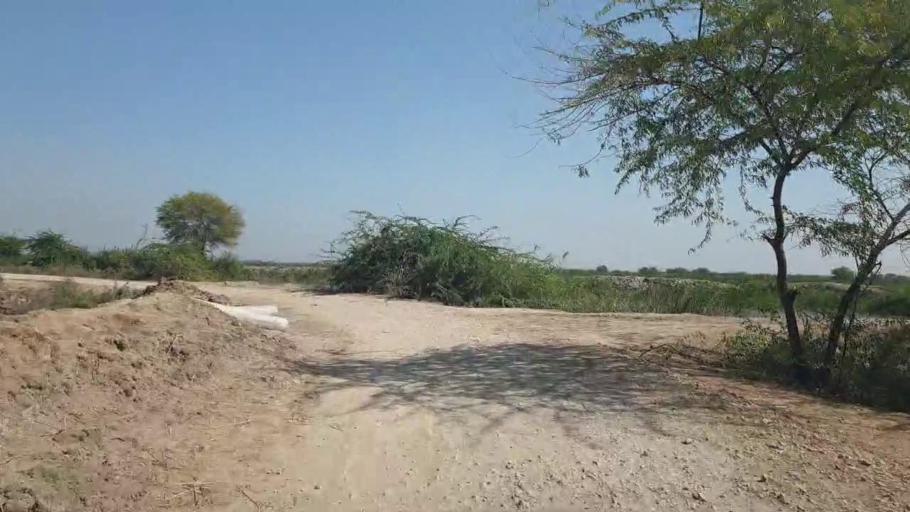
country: PK
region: Sindh
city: Talhar
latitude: 24.7766
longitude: 68.7851
